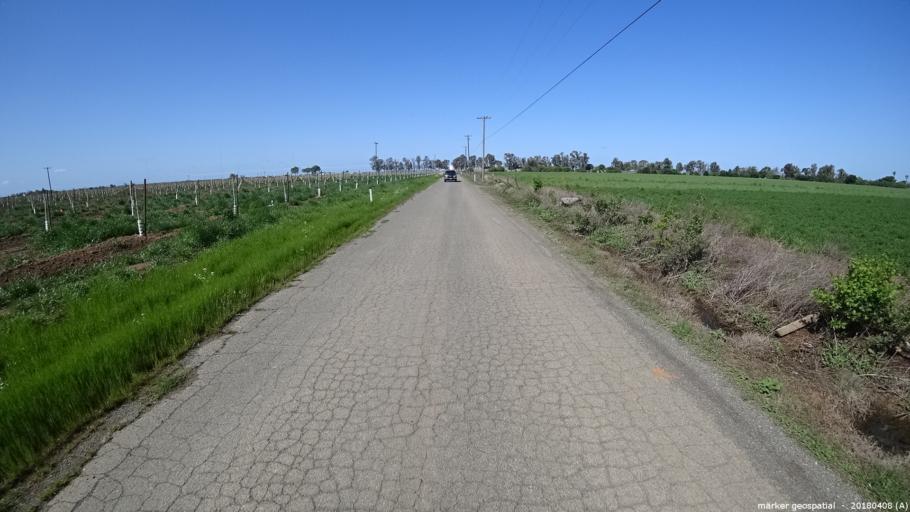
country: US
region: California
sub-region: San Joaquin County
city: Thornton
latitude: 38.3050
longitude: -121.4152
